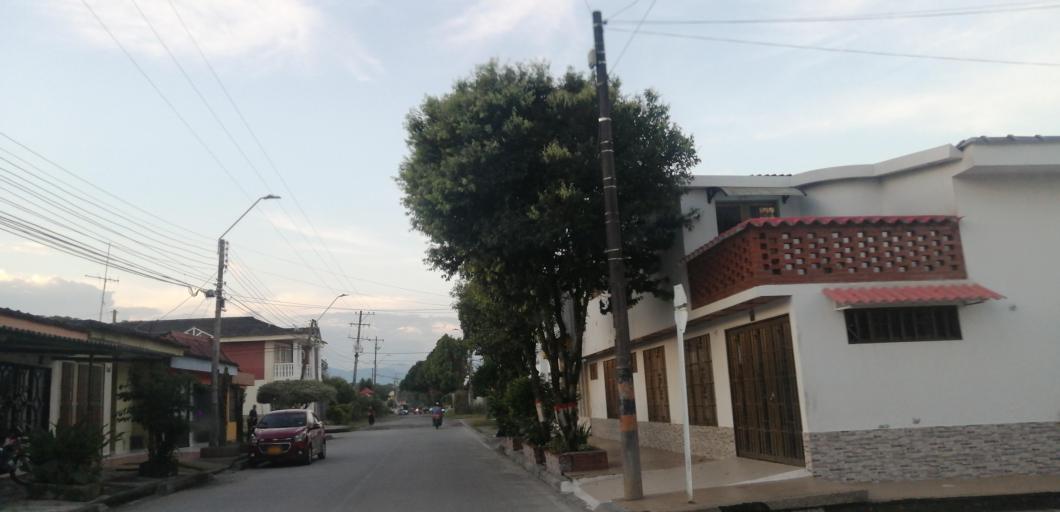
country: CO
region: Meta
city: Acacias
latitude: 3.9948
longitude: -73.7565
